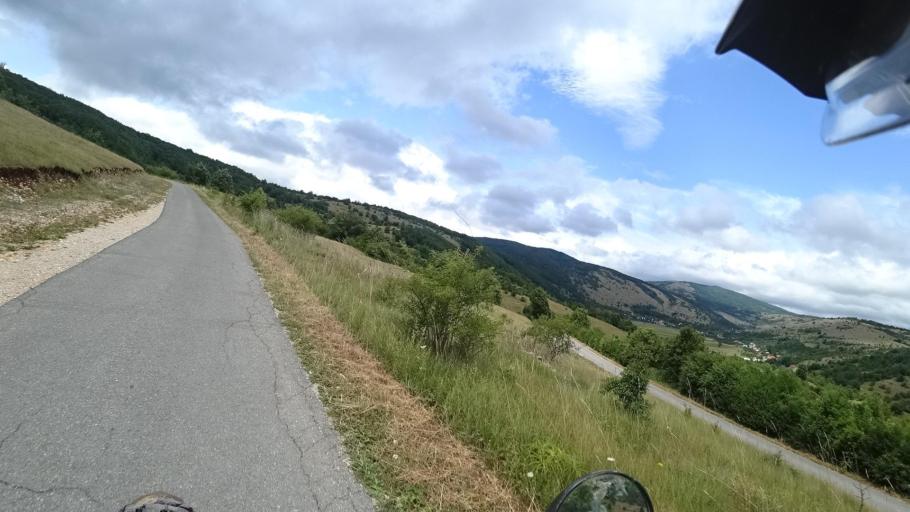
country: HR
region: Licko-Senjska
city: Jezerce
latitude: 44.7245
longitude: 15.5067
